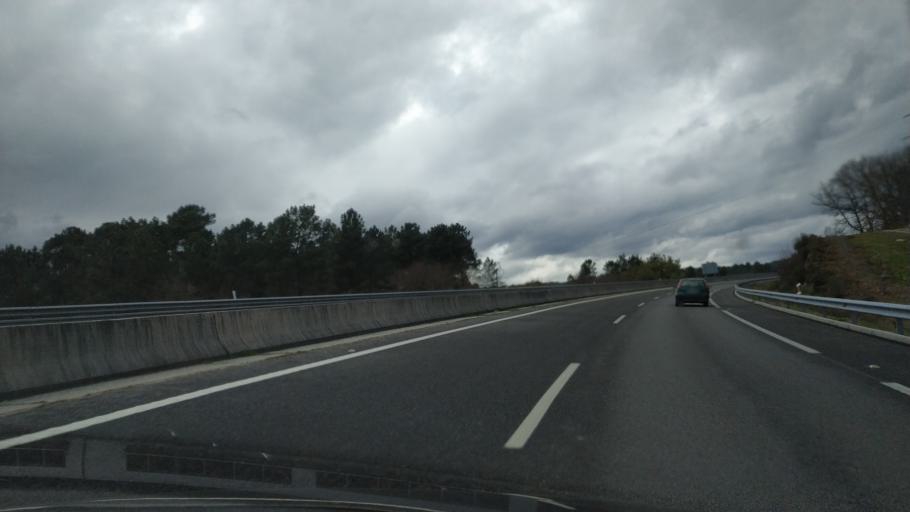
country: ES
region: Galicia
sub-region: Provincia de Ourense
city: Maside
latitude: 42.4155
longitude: -8.0159
